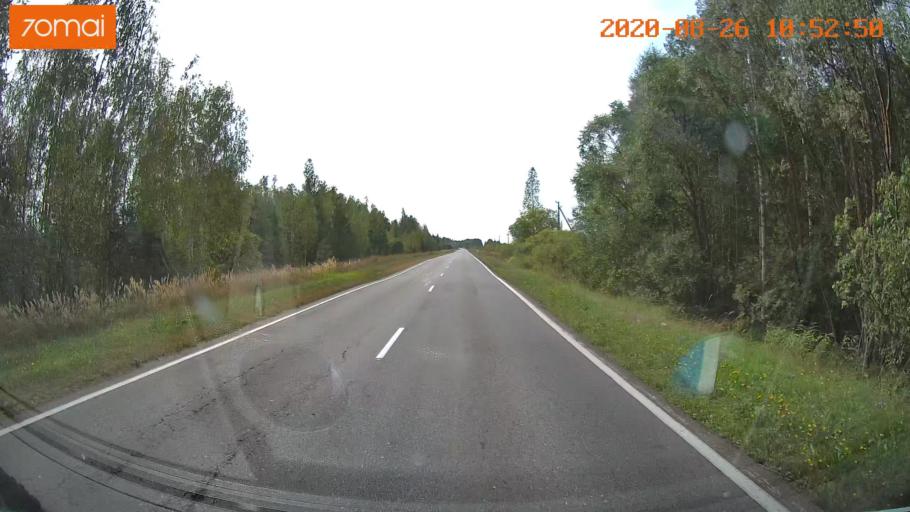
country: RU
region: Rjazan
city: Lashma
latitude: 54.6510
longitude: 41.1527
